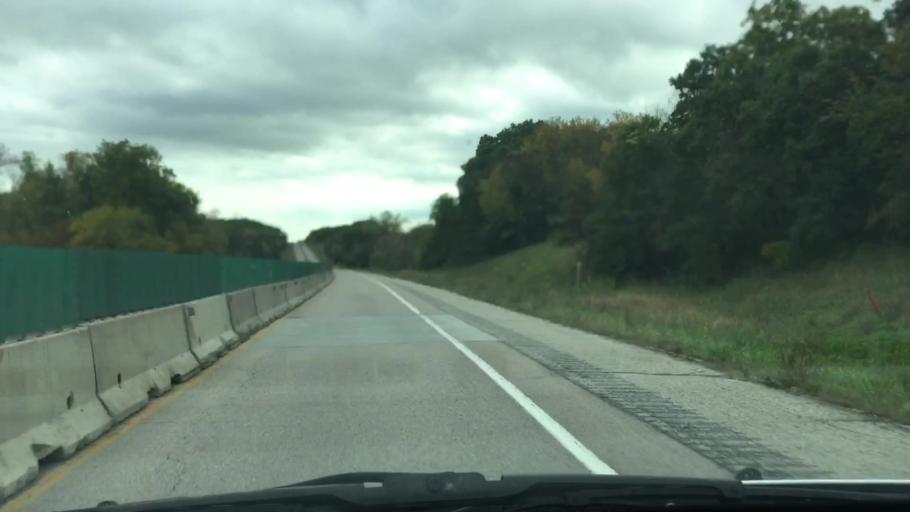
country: US
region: Iowa
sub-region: Decatur County
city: Leon
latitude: 40.7159
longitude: -93.8452
